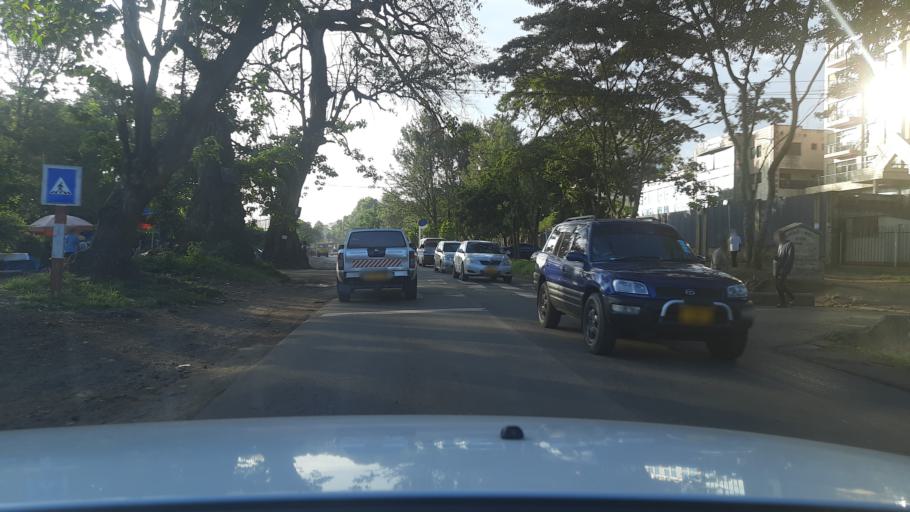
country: TZ
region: Arusha
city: Arusha
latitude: -3.3786
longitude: 36.7051
